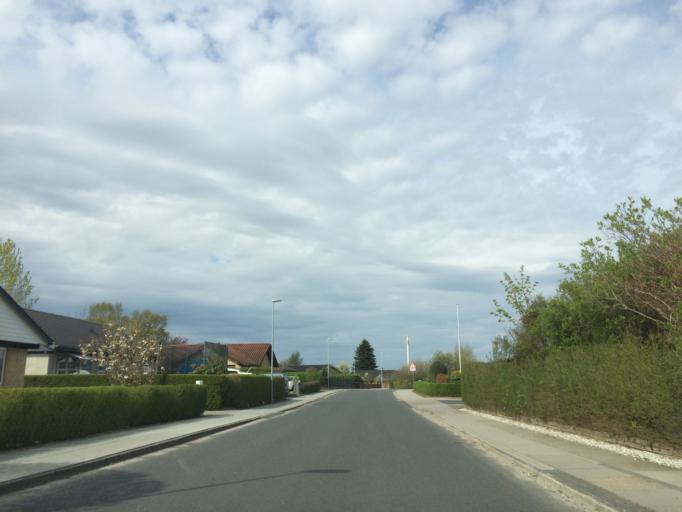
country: DK
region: Central Jutland
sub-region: Viborg Kommune
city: Bjerringbro
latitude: 56.2655
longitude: 9.7298
